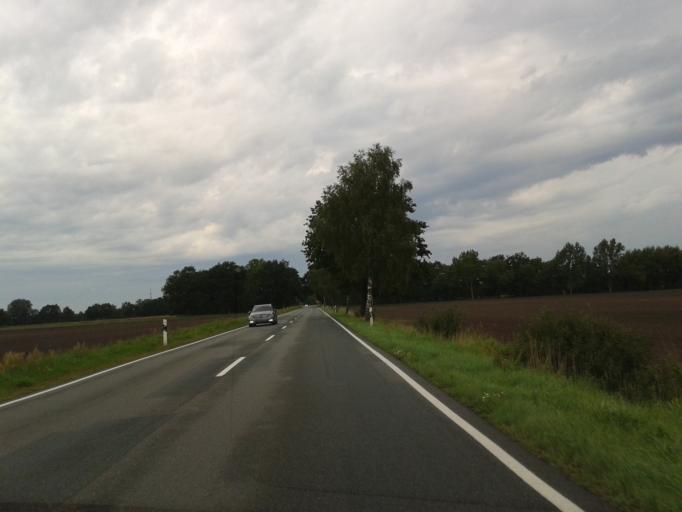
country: DE
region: Lower Saxony
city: Woltersdorf
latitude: 52.9584
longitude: 11.1996
